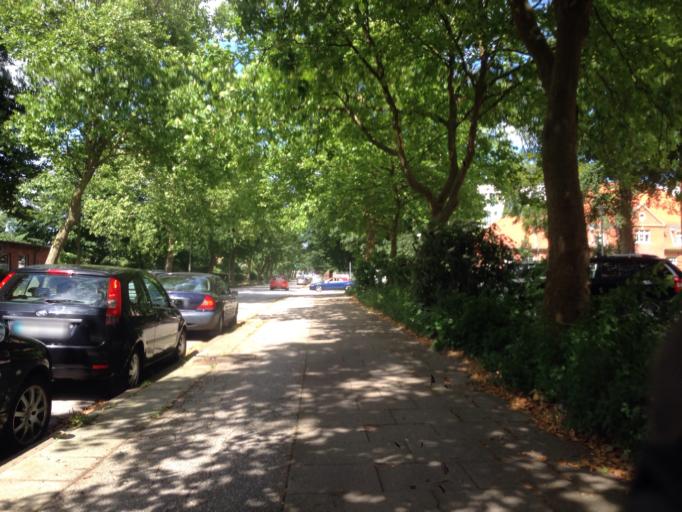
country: DE
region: Hamburg
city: Barmbek-Nord
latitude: 53.6033
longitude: 10.0352
